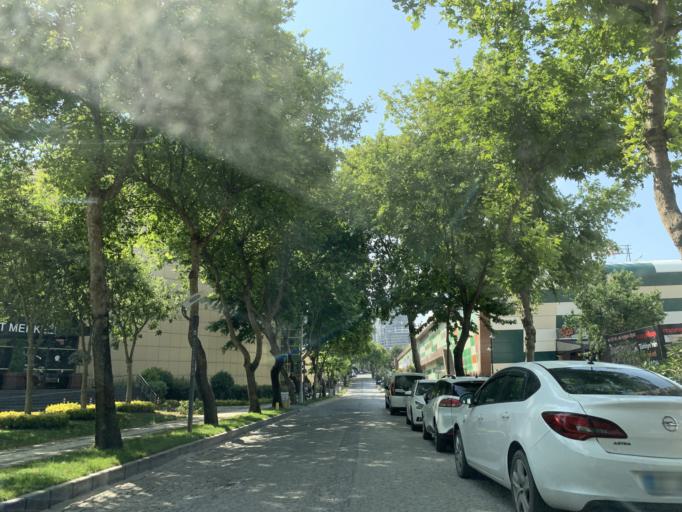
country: TR
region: Istanbul
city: Esenyurt
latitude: 41.0669
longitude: 28.6919
